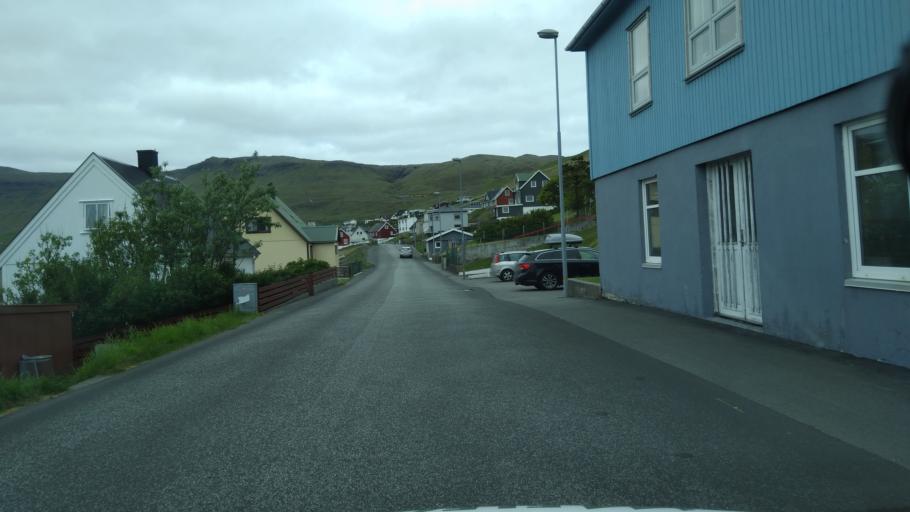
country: FO
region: Suduroy
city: Tvoroyri
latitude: 61.5599
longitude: -6.8242
